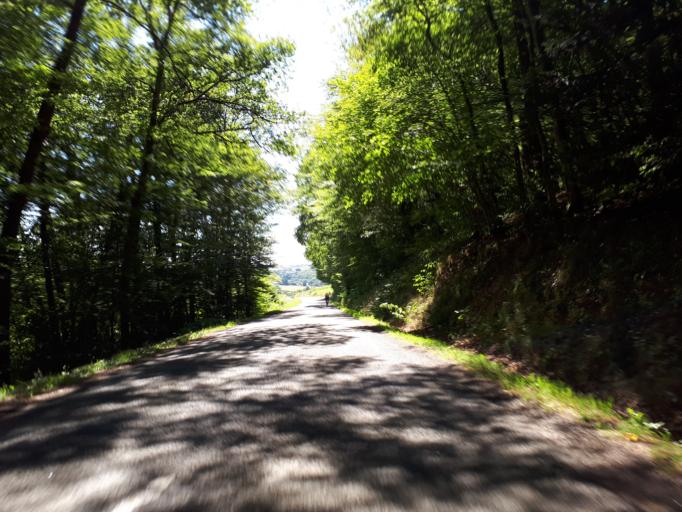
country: FR
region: Rhone-Alpes
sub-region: Departement de la Loire
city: Panissieres
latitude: 45.8168
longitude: 4.3110
